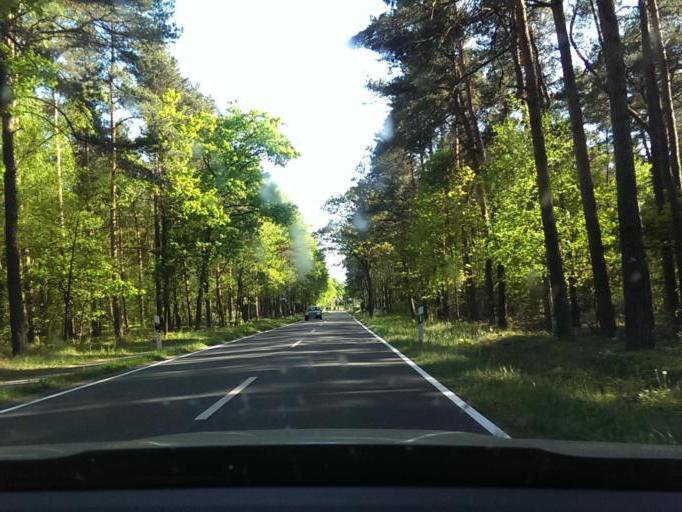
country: DE
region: Lower Saxony
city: Wietze
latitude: 52.6654
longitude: 9.8380
